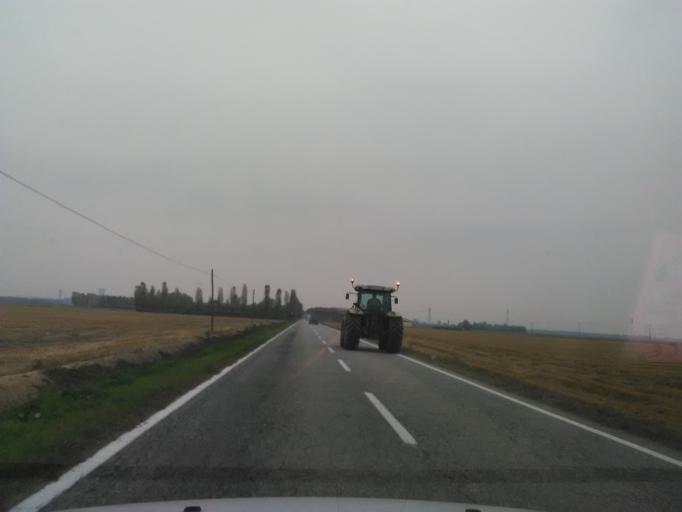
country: IT
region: Piedmont
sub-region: Provincia di Vercelli
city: Fontanetto Po
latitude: 45.2483
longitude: 8.1737
